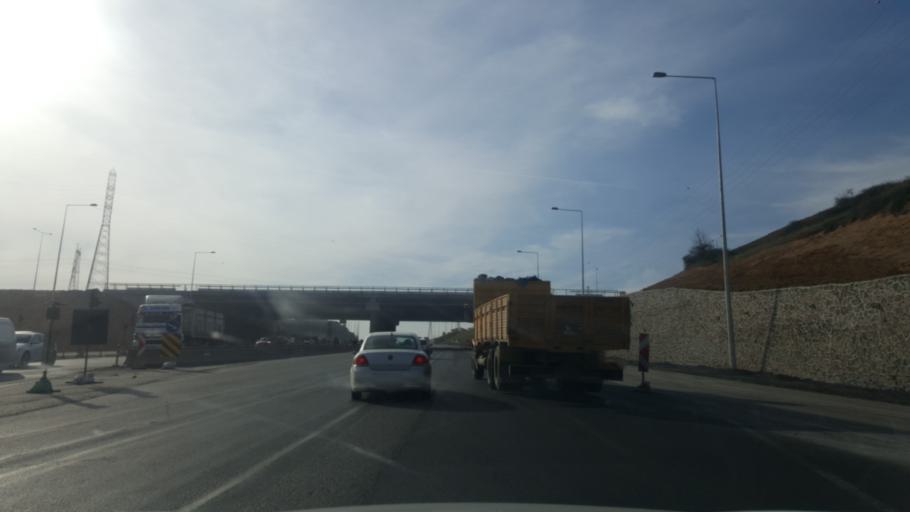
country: TR
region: Kocaeli
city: Tavsanli
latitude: 40.8105
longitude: 29.5226
